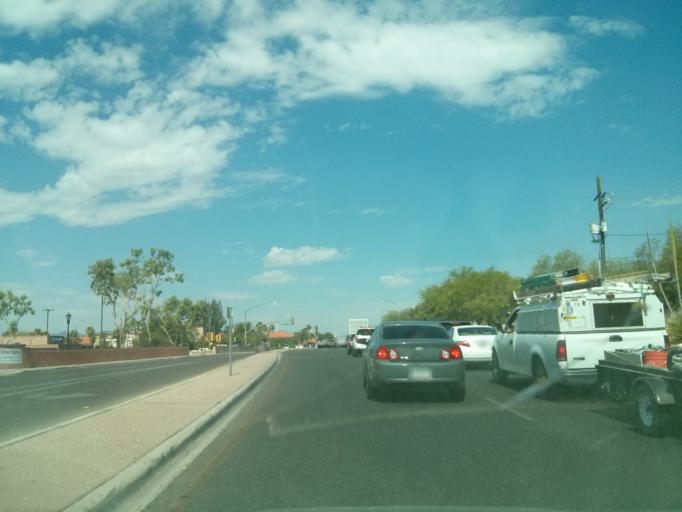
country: US
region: Arizona
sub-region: Pima County
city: Catalina Foothills
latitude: 32.2871
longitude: -110.9421
